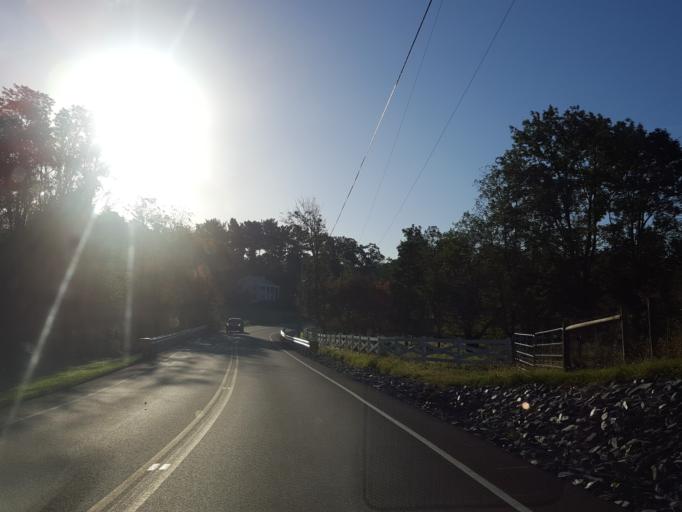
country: US
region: Pennsylvania
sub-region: York County
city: Windsor
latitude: 39.9561
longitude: -76.6084
